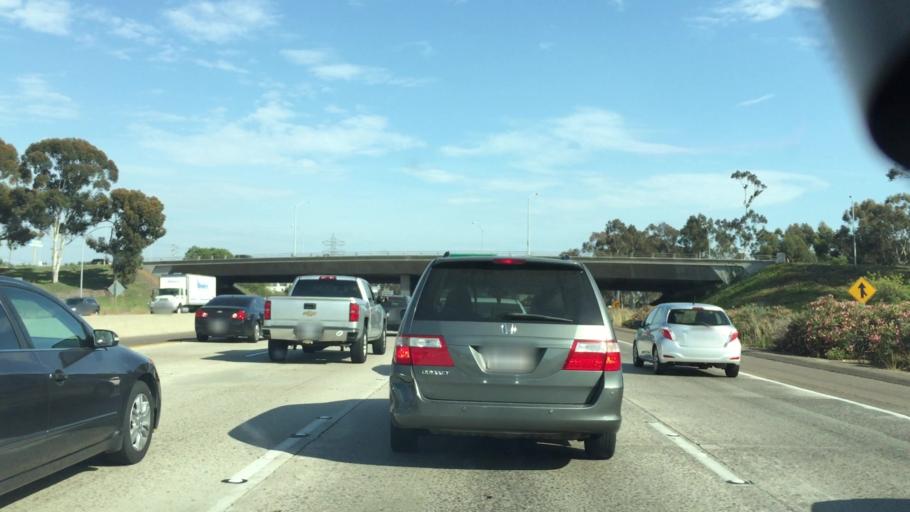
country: US
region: California
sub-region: San Diego County
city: San Diego
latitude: 32.8230
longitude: -117.1634
